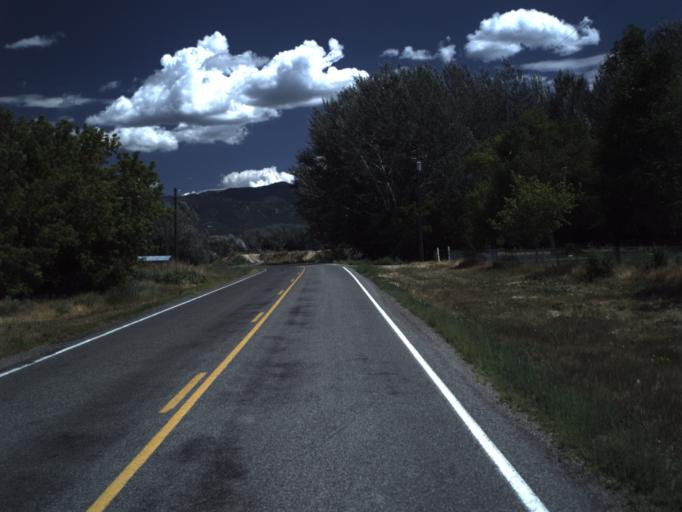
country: US
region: Utah
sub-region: Sanpete County
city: Moroni
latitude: 39.4810
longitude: -111.5156
